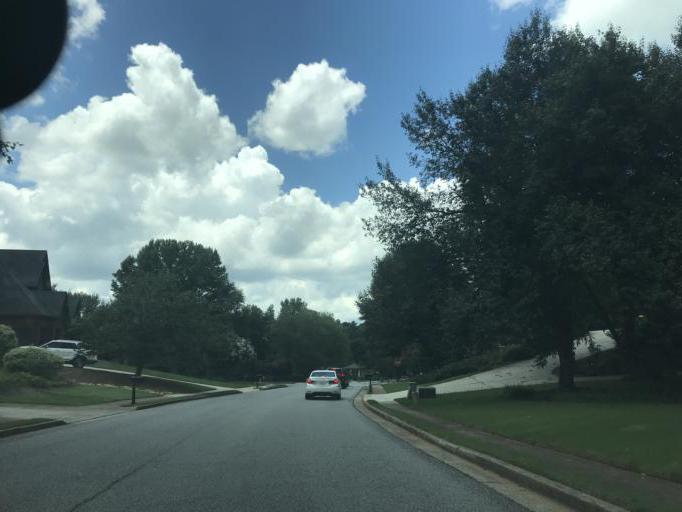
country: US
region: Georgia
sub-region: Fulton County
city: Johns Creek
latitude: 34.0751
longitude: -84.1704
